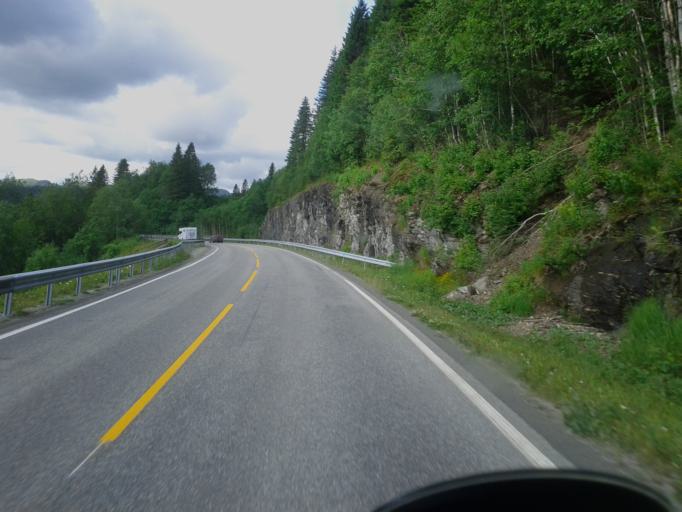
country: NO
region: Nord-Trondelag
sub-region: Grong
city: Grong
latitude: 64.5370
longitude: 12.4202
